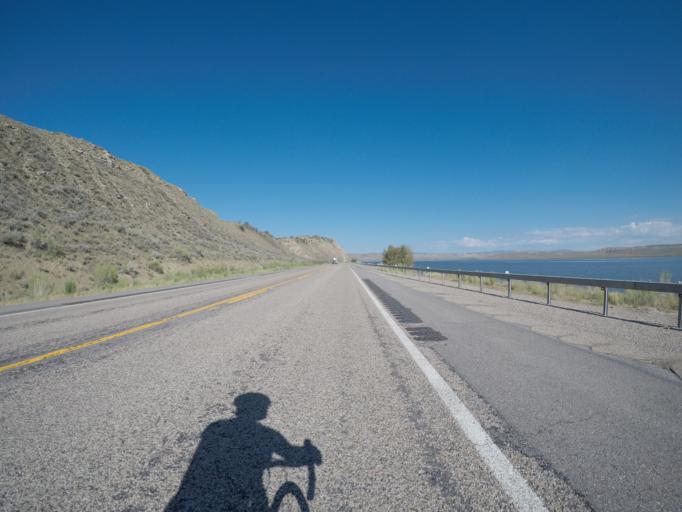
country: US
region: Wyoming
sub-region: Sublette County
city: Marbleton
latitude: 42.1119
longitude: -110.1457
